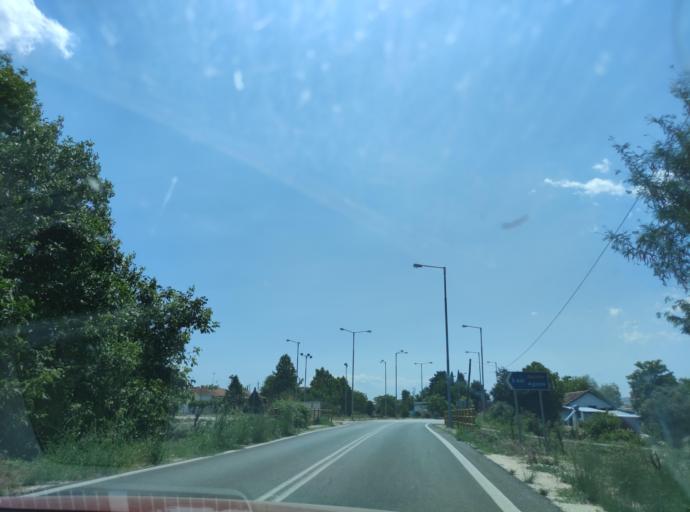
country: GR
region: Central Macedonia
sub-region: Nomos Serron
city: Alistrati
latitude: 41.0078
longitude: 23.9420
